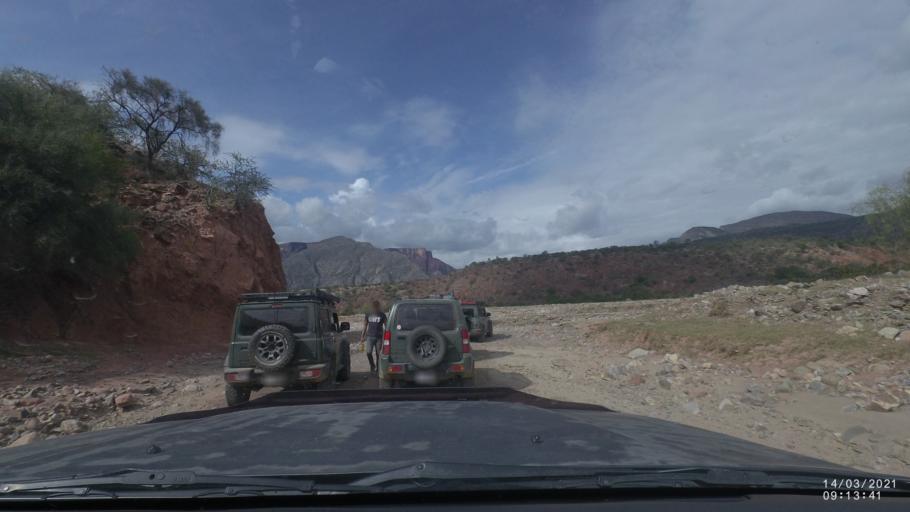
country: BO
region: Cochabamba
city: Cliza
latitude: -17.9490
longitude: -65.8529
